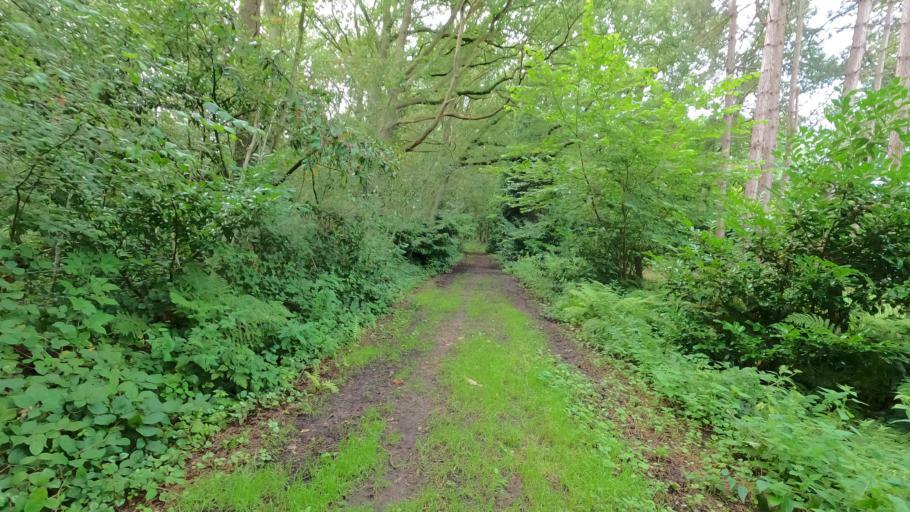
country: BE
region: Flanders
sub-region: Provincie Antwerpen
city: Heist-op-den-Berg
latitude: 51.0934
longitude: 4.7029
